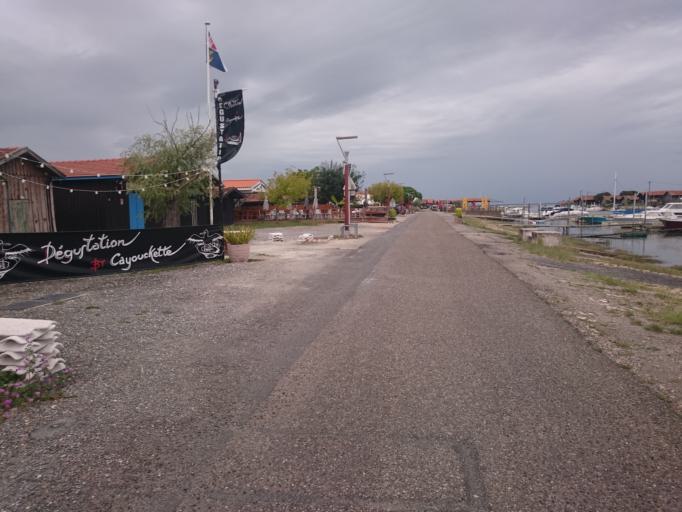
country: FR
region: Aquitaine
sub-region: Departement de la Gironde
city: Gujan-Mestras
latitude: 44.6418
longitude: -1.0727
